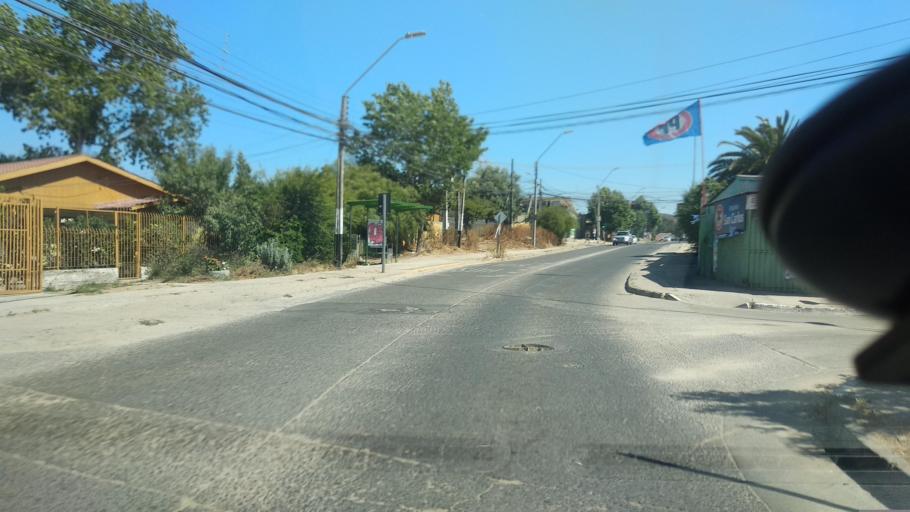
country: CL
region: Valparaiso
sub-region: Provincia de Marga Marga
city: Villa Alemana
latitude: -33.0579
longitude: -71.3725
